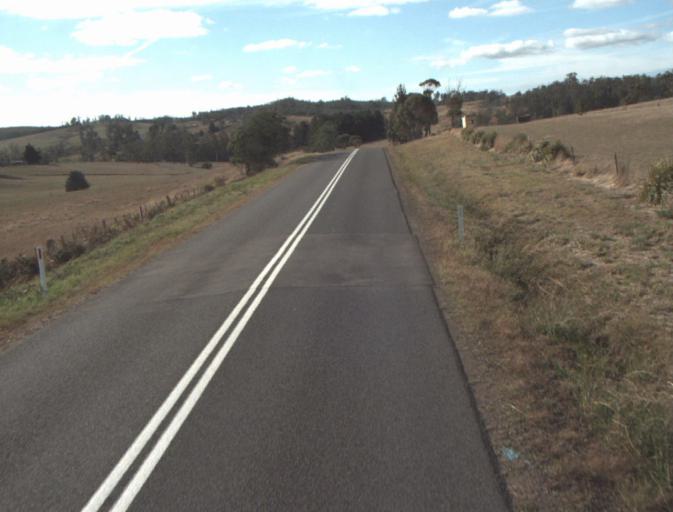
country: AU
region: Tasmania
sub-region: Launceston
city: Mayfield
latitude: -41.2146
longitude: 147.1213
